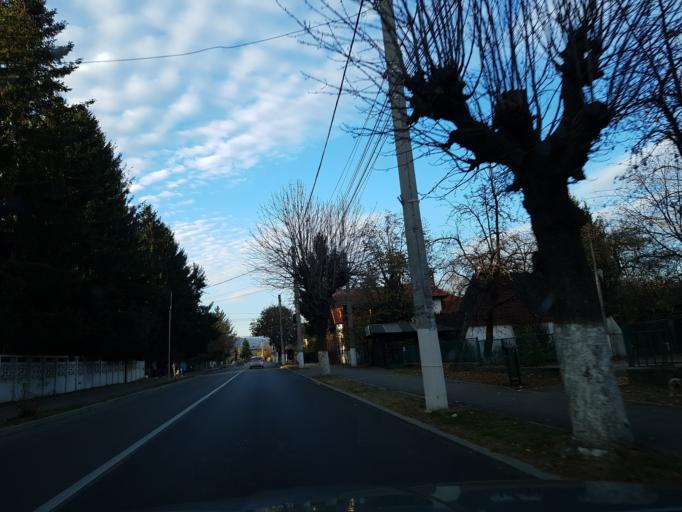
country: RO
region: Prahova
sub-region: Oras Breaza
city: Breaza
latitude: 45.1826
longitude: 25.6671
